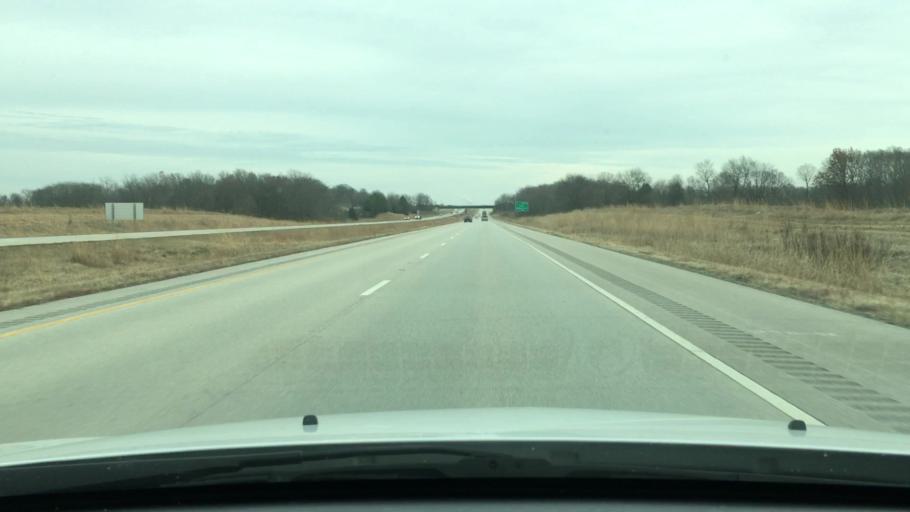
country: US
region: Illinois
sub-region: Sangamon County
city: Jerome
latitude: 39.7517
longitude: -89.7707
